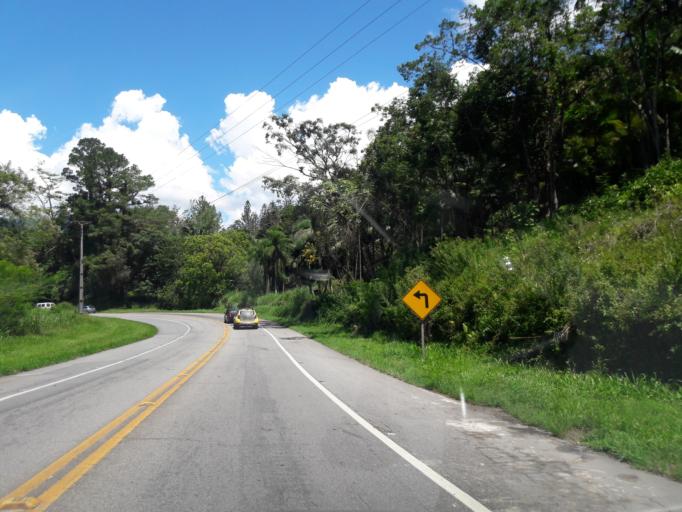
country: BR
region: Parana
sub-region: Antonina
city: Antonina
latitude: -25.5132
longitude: -48.8075
